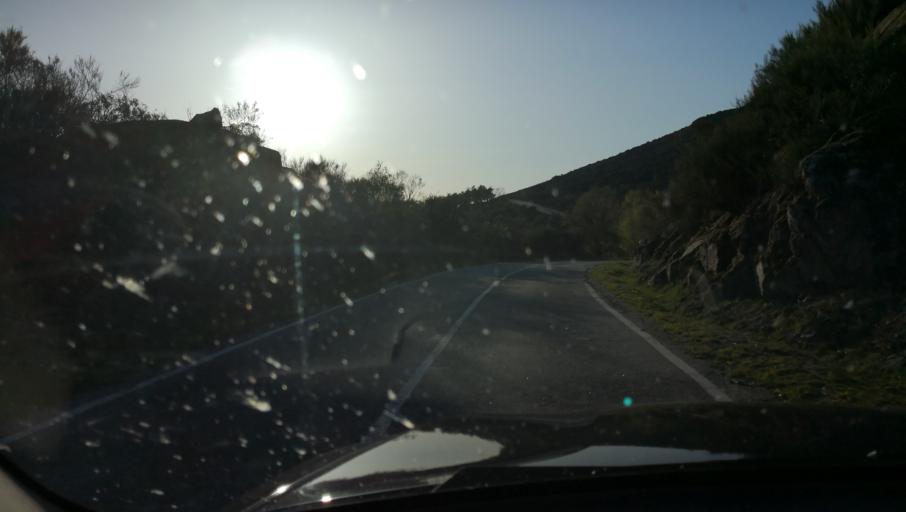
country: PT
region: Vila Real
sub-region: Vila Real
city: Vila Real
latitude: 41.3781
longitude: -7.8124
